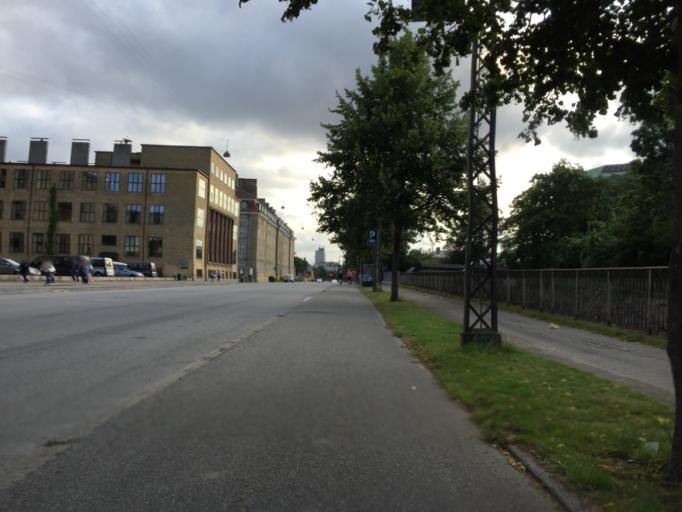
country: DK
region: Capital Region
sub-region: Kobenhavn
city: Christianshavn
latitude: 55.6890
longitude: 12.5815
